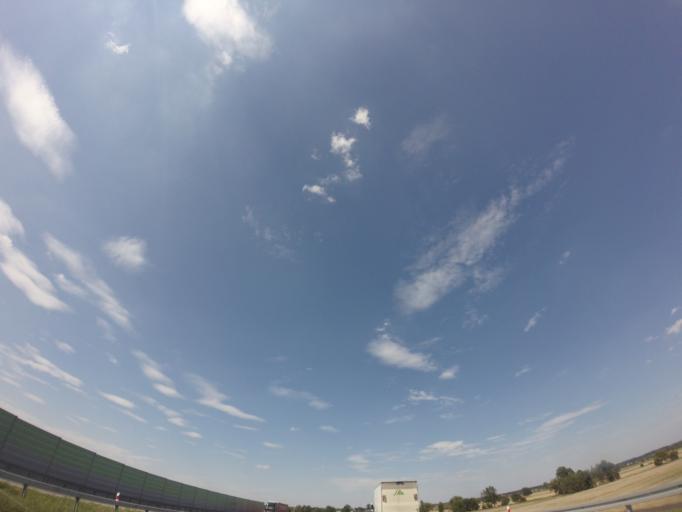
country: PL
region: Lower Silesian Voivodeship
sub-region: Legnica
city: Legnica
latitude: 51.2373
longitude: 16.1433
